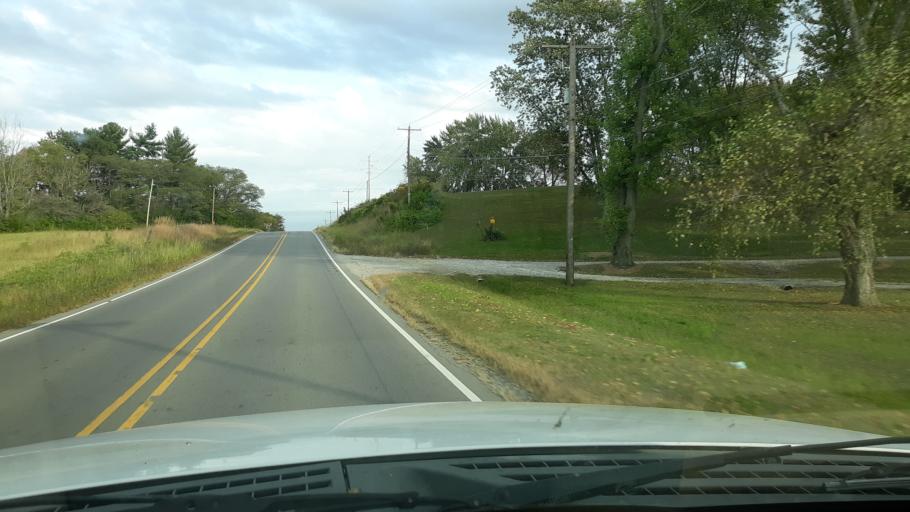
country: US
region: Illinois
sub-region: Saline County
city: Eldorado
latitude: 37.8220
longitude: -88.4939
